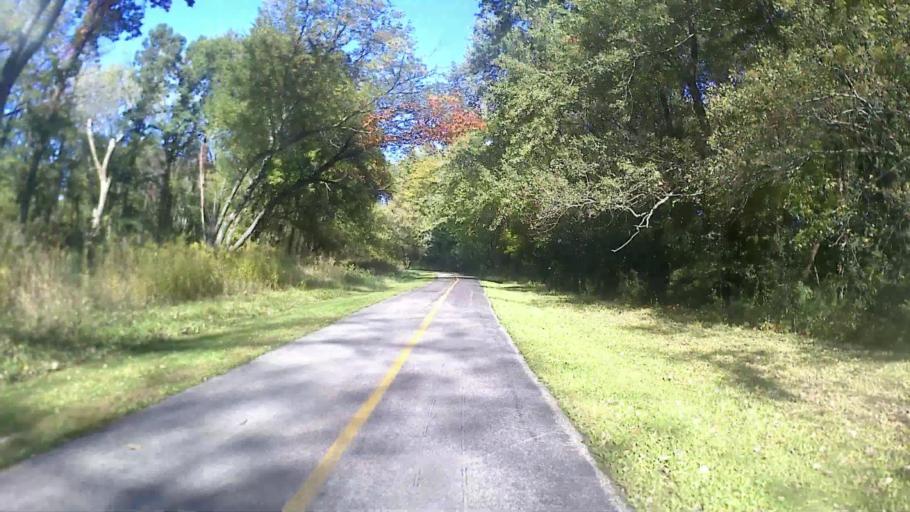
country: US
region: Illinois
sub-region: DuPage County
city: Itasca
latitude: 42.0265
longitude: -88.0189
